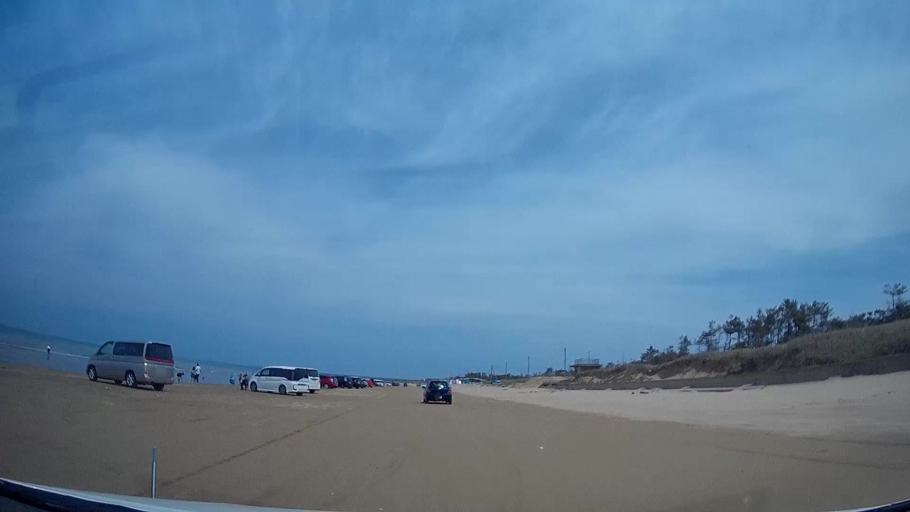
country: JP
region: Ishikawa
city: Hakui
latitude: 36.8396
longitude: 136.7492
